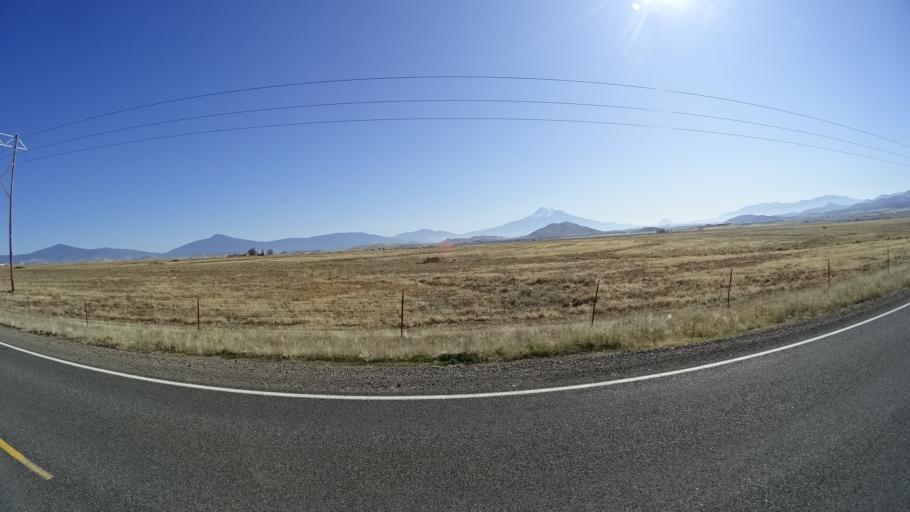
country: US
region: California
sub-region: Siskiyou County
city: Montague
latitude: 41.7618
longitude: -122.5598
